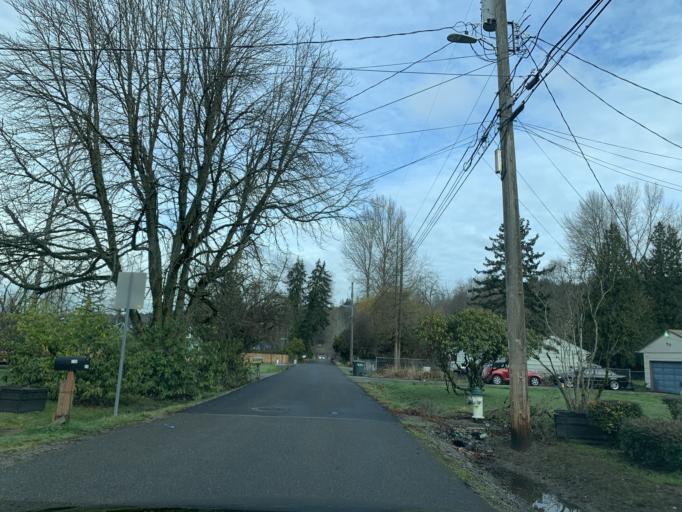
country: US
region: Washington
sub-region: Pierce County
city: Fife Heights
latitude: 47.2549
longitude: -122.3548
